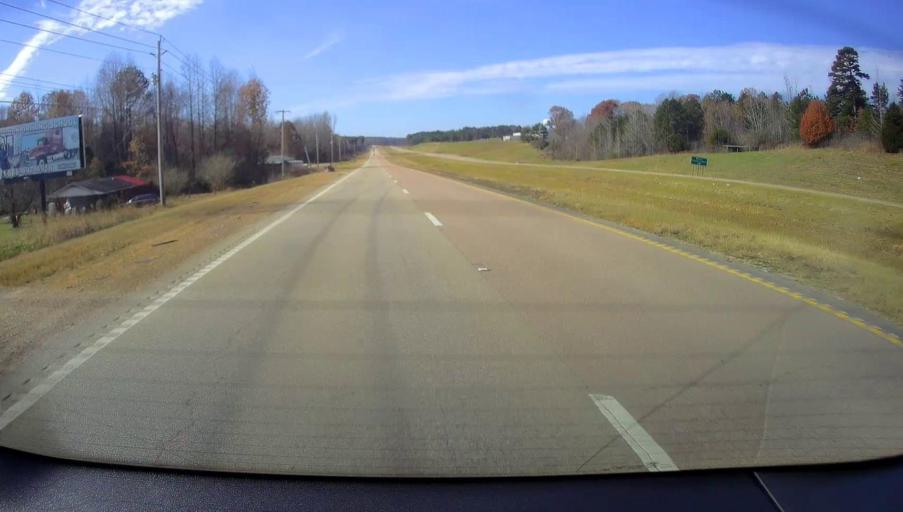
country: US
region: Mississippi
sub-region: Tippah County
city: Ripley
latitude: 34.9504
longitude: -88.9257
